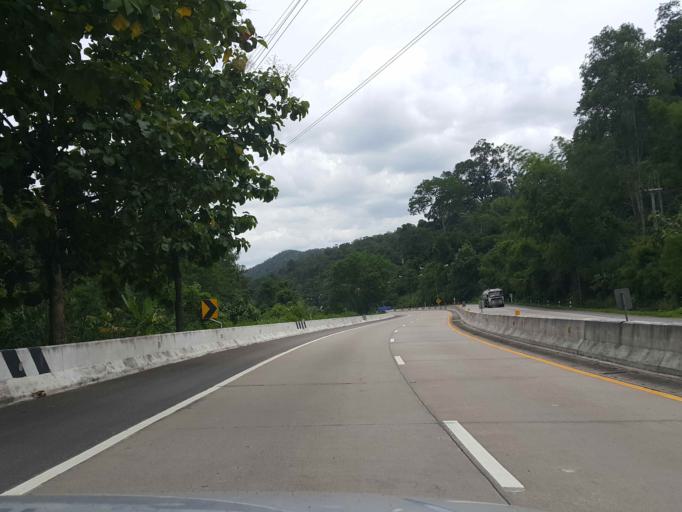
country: TH
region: Lamphun
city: Mae Tha
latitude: 18.3970
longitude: 99.2154
